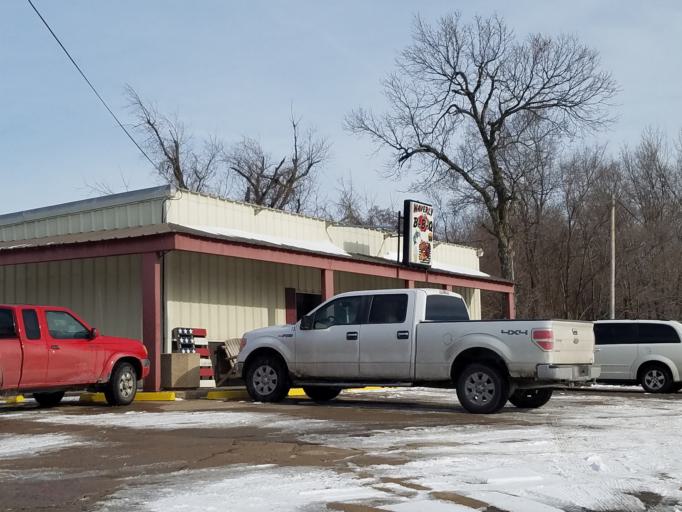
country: US
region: Missouri
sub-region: Carroll County
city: Carrollton
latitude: 39.2072
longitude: -93.5133
